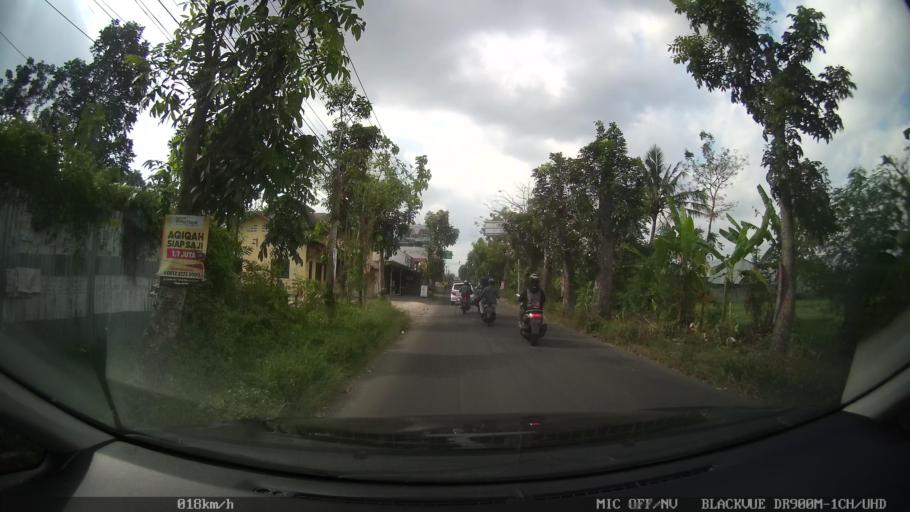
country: ID
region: Daerah Istimewa Yogyakarta
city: Melati
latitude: -7.7462
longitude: 110.3487
